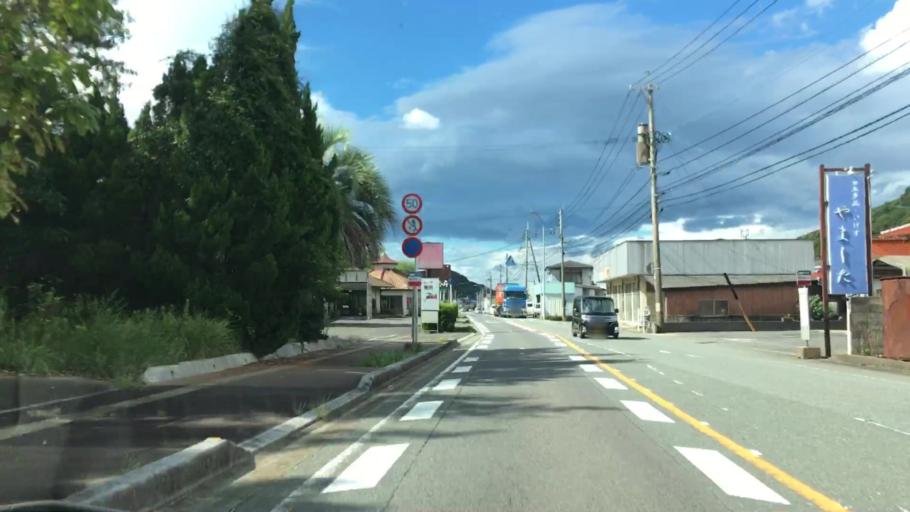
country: JP
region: Saga Prefecture
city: Imaricho-ko
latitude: 33.1885
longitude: 129.8522
